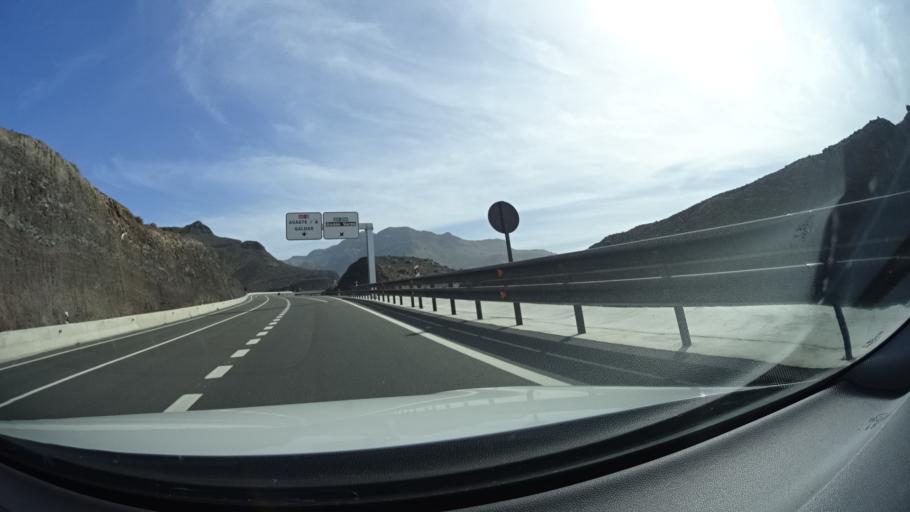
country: ES
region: Canary Islands
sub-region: Provincia de Las Palmas
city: San Nicolas
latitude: 28.0082
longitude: -15.7923
